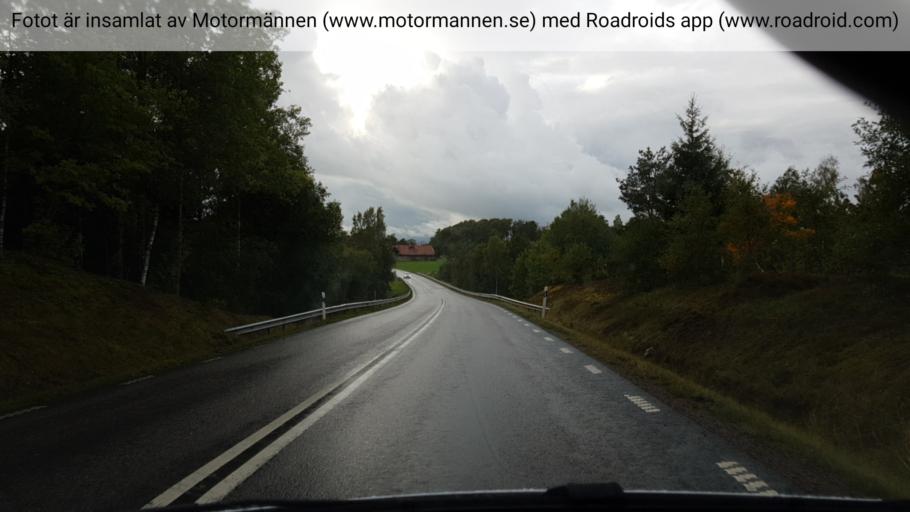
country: SE
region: Joenkoeping
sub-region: Mullsjo Kommun
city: Mullsjoe
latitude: 58.0722
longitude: 13.8041
